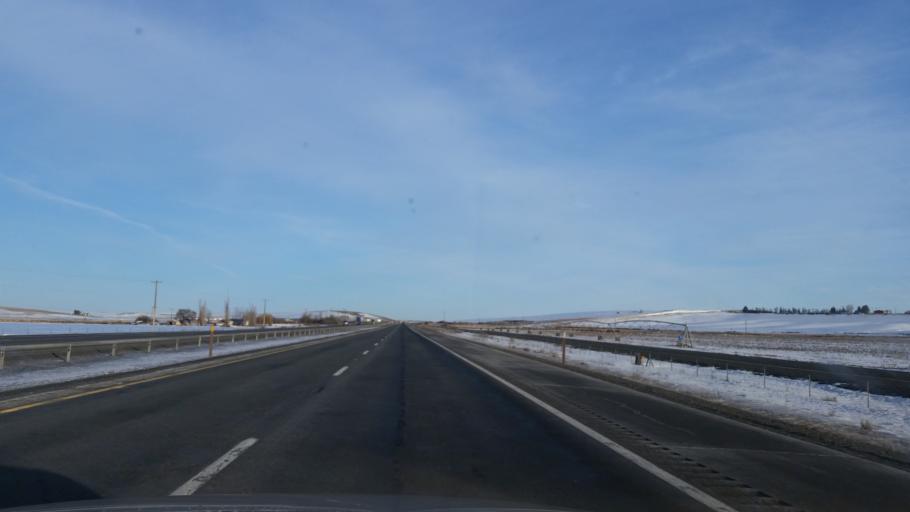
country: US
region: Washington
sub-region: Grant County
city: Warden
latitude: 47.0854
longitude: -119.0302
